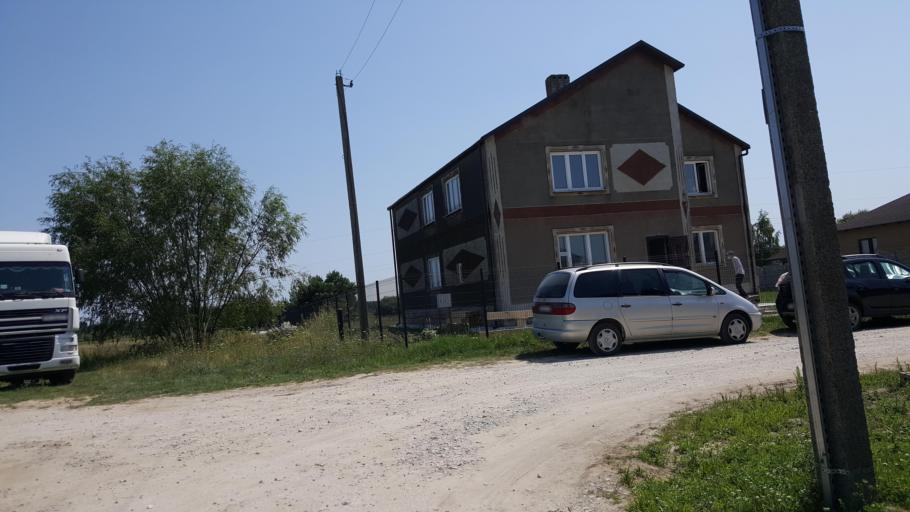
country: BY
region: Brest
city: Zhabinka
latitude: 52.1860
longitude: 23.9990
